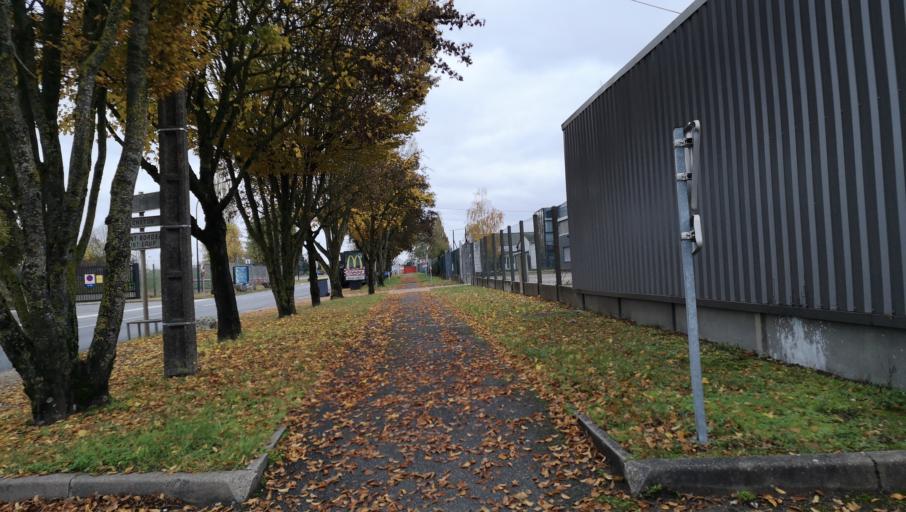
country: FR
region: Centre
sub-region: Departement du Loiret
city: Semoy
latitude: 47.9191
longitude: 1.9564
